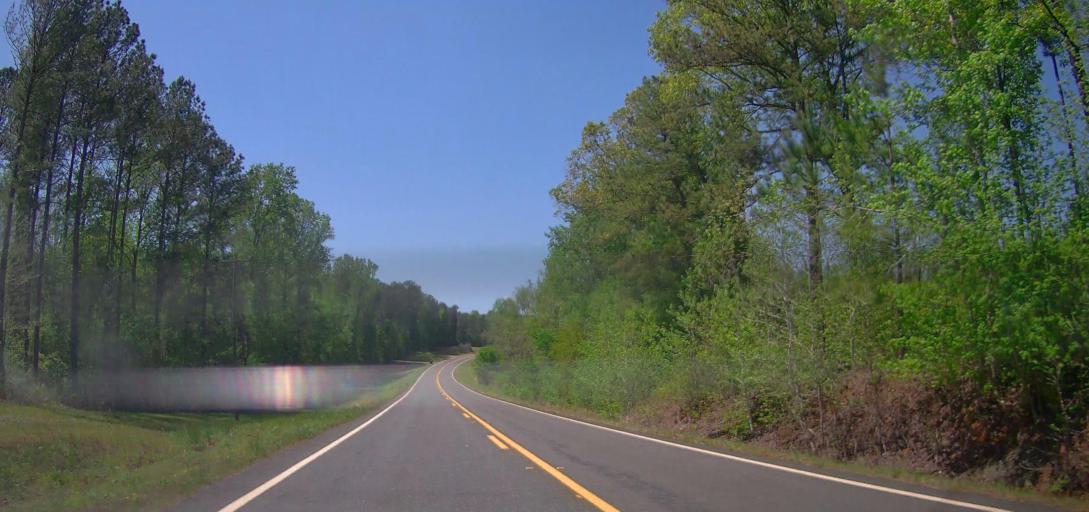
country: US
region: Georgia
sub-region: Jasper County
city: Monticello
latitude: 33.2640
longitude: -83.5789
